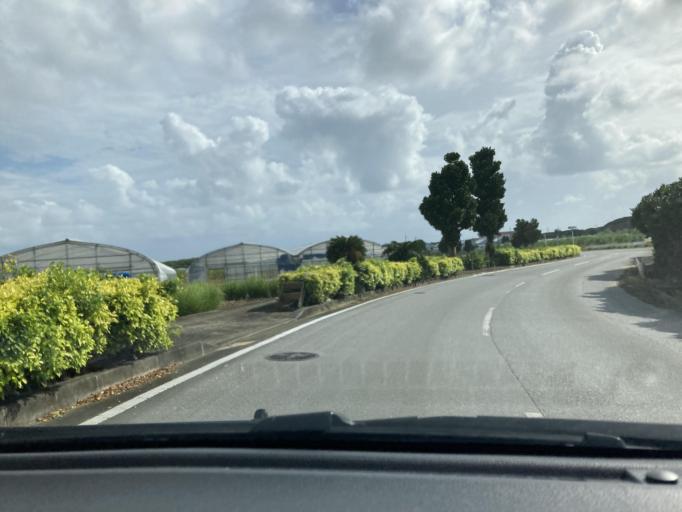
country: JP
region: Okinawa
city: Itoman
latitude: 26.0910
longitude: 127.6942
